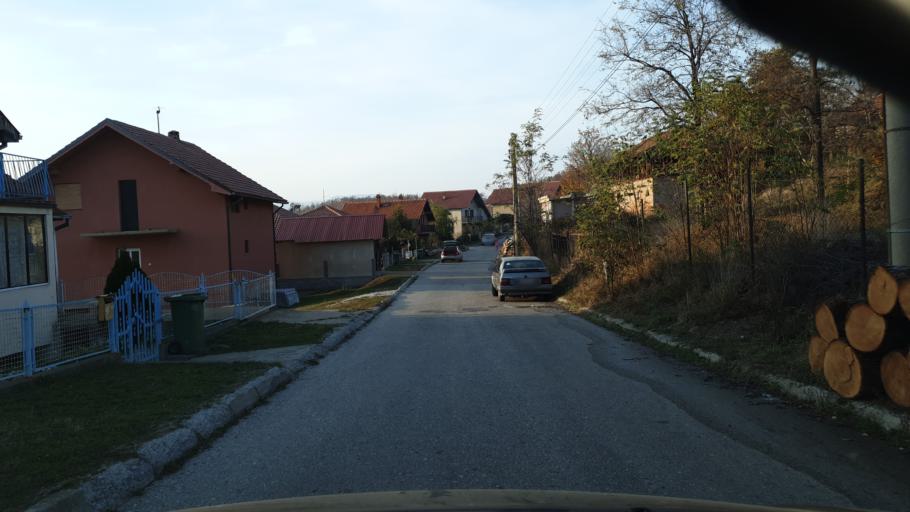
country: RS
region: Central Serbia
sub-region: Borski Okrug
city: Bor
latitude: 44.0584
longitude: 22.0800
